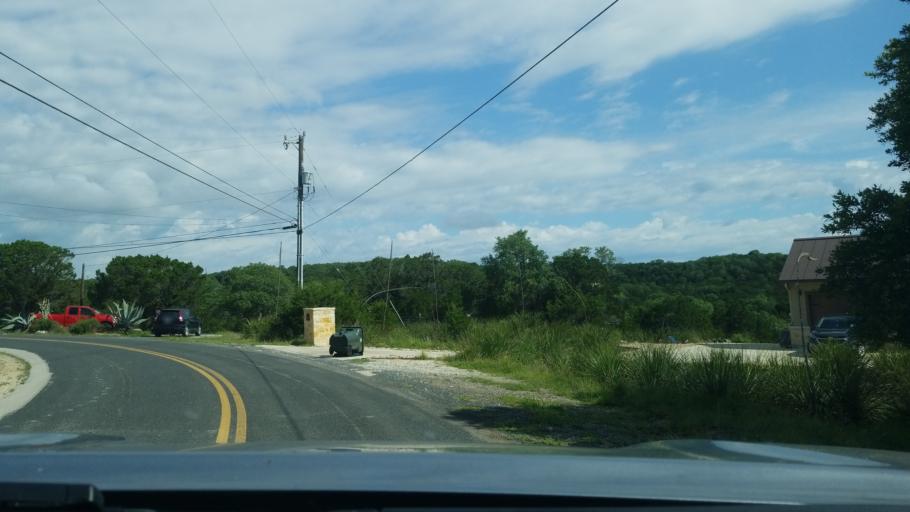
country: US
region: Texas
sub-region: Comal County
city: Bulverde
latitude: 29.7652
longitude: -98.4421
